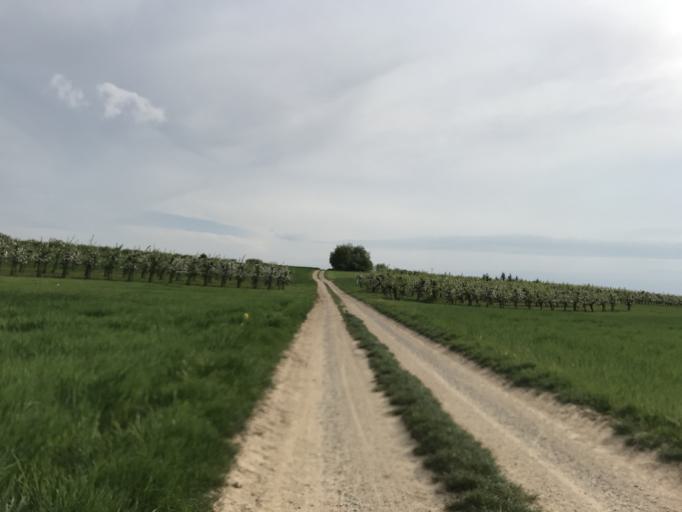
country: DE
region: Rheinland-Pfalz
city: Schwabenheim
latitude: 49.9492
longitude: 8.1016
